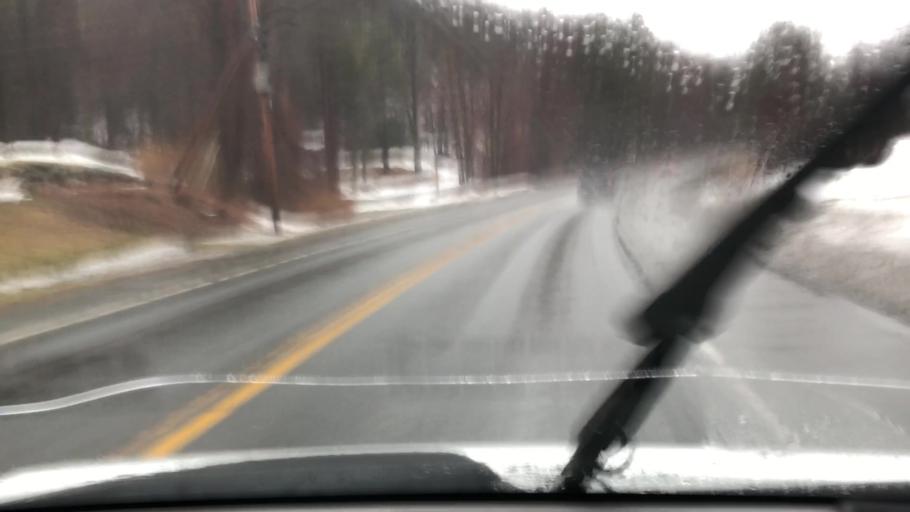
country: US
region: Massachusetts
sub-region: Franklin County
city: Shelburne Falls
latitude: 42.5909
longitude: -72.7197
